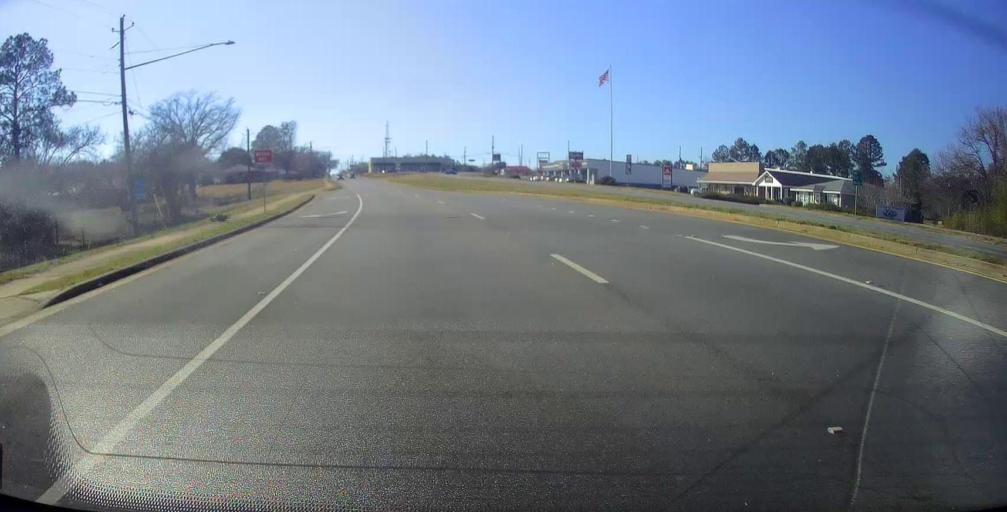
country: US
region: Georgia
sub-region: Sumter County
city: Americus
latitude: 32.0712
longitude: -84.2098
